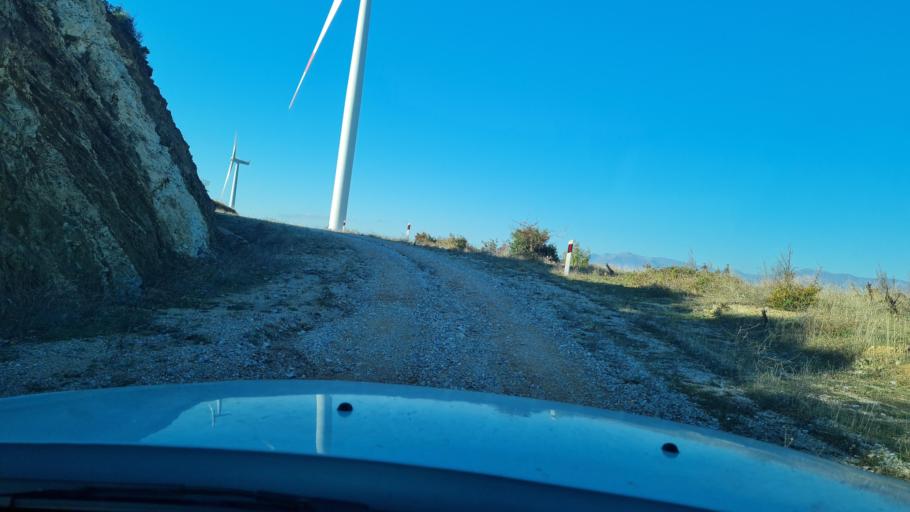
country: MK
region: Bogdanci
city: Bogdanci
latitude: 41.2170
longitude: 22.5449
